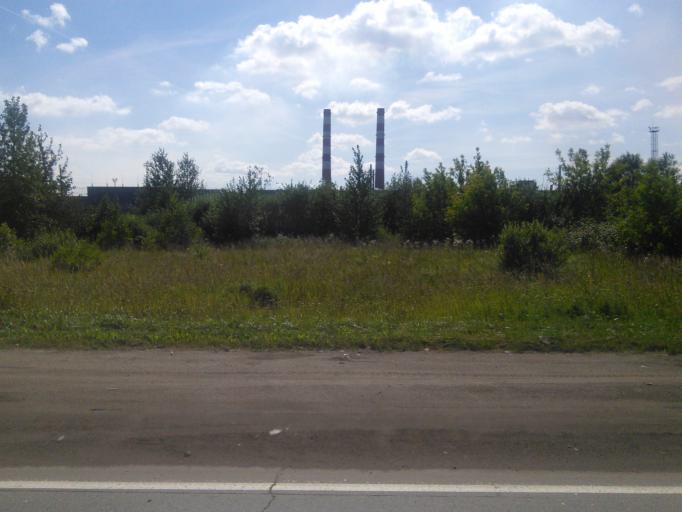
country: RU
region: Vologda
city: Cherepovets
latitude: 59.1535
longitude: 37.8871
